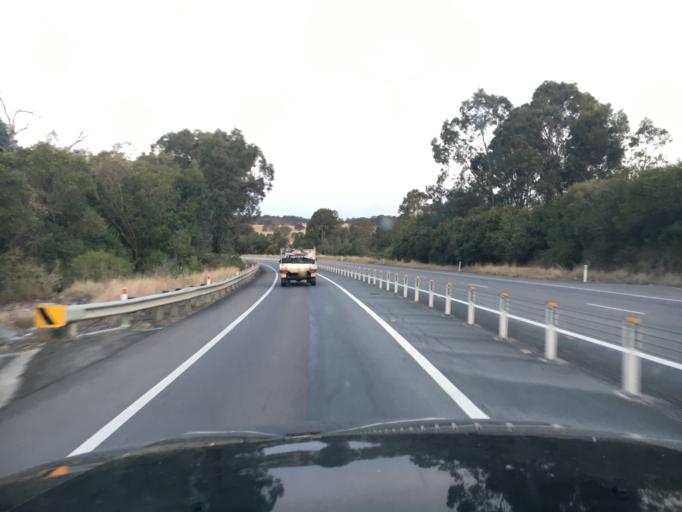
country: AU
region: New South Wales
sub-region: Cessnock
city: Greta
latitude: -32.7071
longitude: 151.4194
